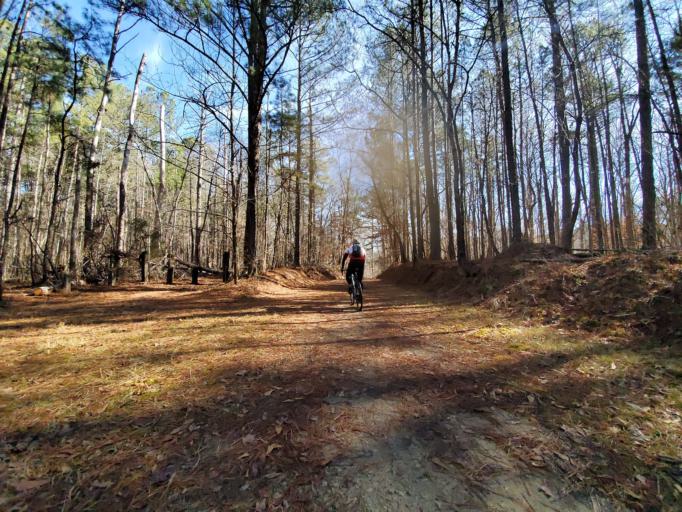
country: US
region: Georgia
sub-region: Fulton County
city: Chattahoochee Hills
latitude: 33.5725
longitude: -84.7249
